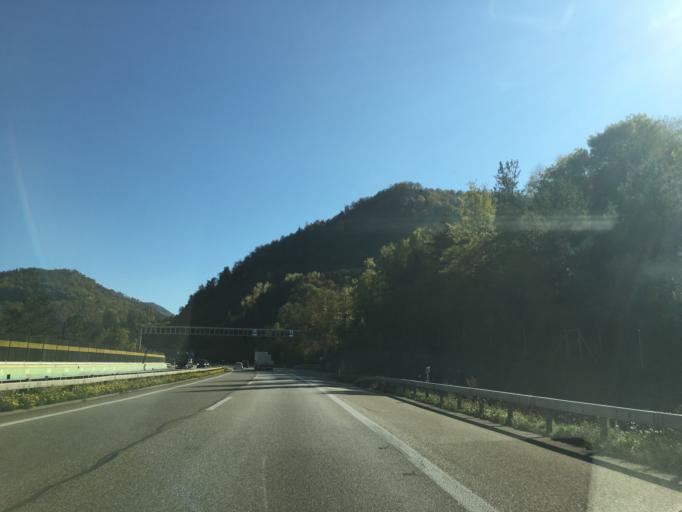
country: CH
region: Basel-Landschaft
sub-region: Bezirk Waldenburg
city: Diegten
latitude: 47.4022
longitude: 7.8077
